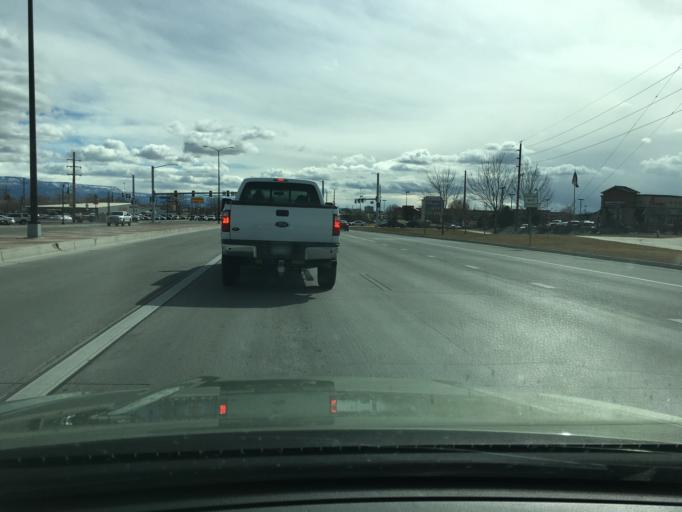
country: US
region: Colorado
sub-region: Mesa County
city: Grand Junction
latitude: 39.0813
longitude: -108.5851
